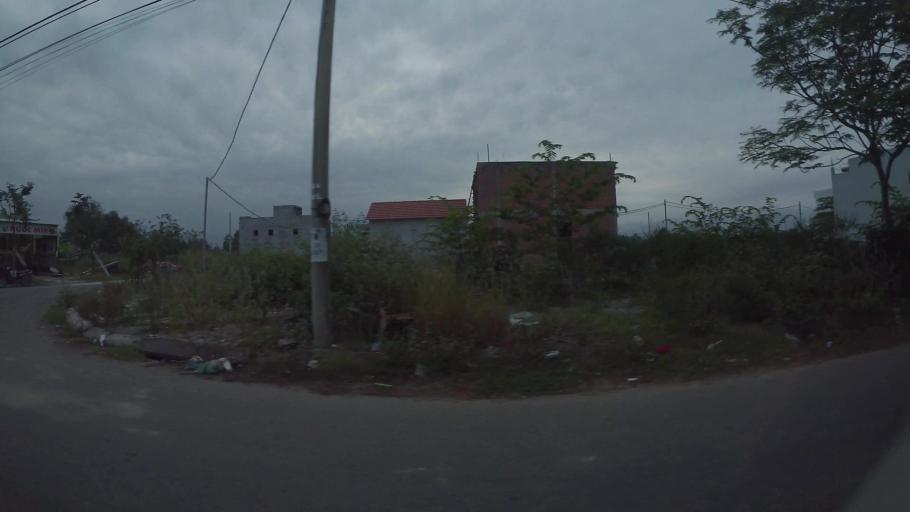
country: VN
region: Da Nang
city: Lien Chieu
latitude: 16.0728
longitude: 108.1080
